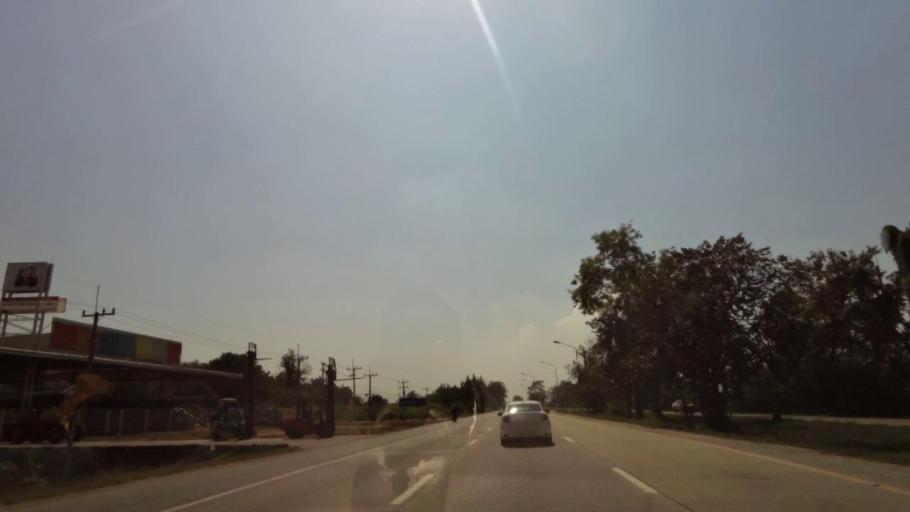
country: TH
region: Phichit
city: Wachira Barami
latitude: 16.5978
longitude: 100.1474
